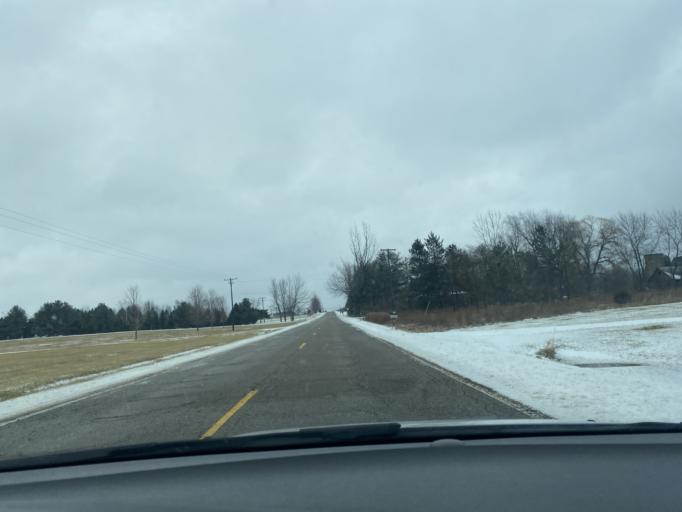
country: US
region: Michigan
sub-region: Lapeer County
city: North Branch
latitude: 43.2088
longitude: -83.1507
